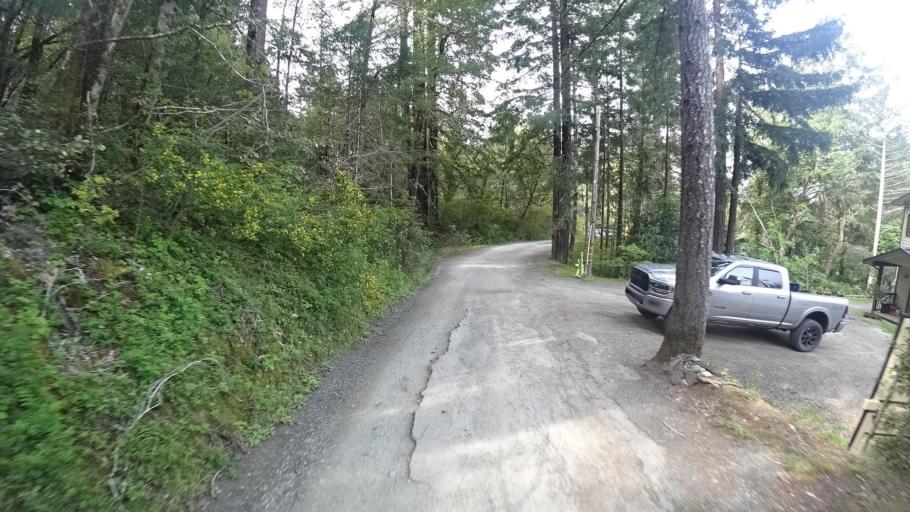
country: US
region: California
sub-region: Humboldt County
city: Redway
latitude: 40.2371
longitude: -123.8170
